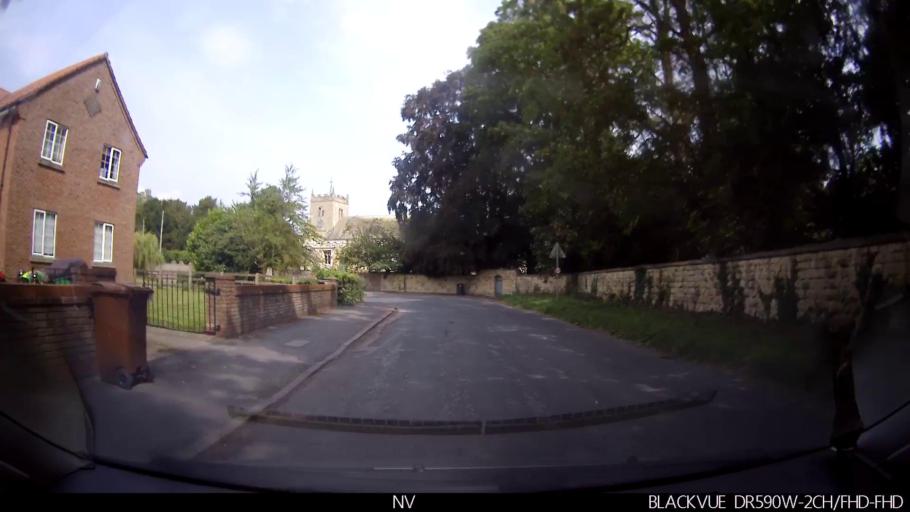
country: GB
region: England
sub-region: North Yorkshire
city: Great Habton
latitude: 54.2052
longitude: -0.8068
